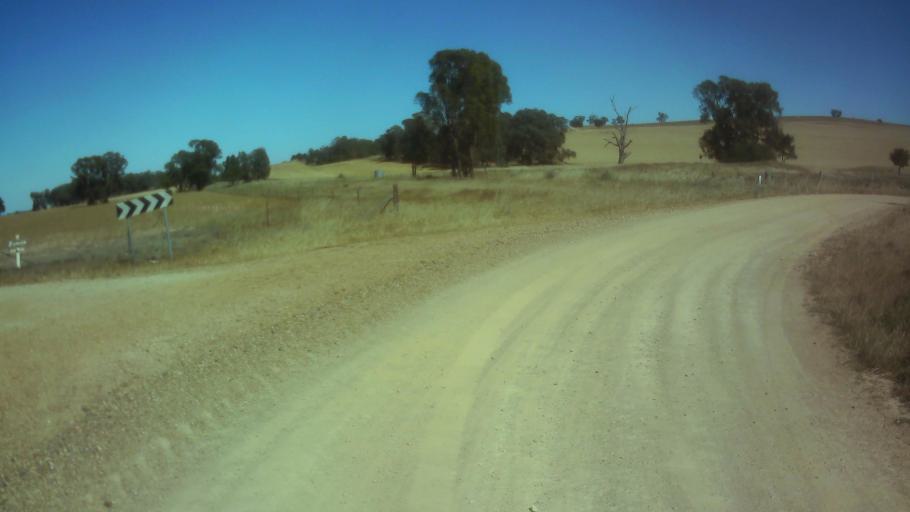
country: AU
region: New South Wales
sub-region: Weddin
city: Grenfell
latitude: -33.9947
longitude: 148.3568
